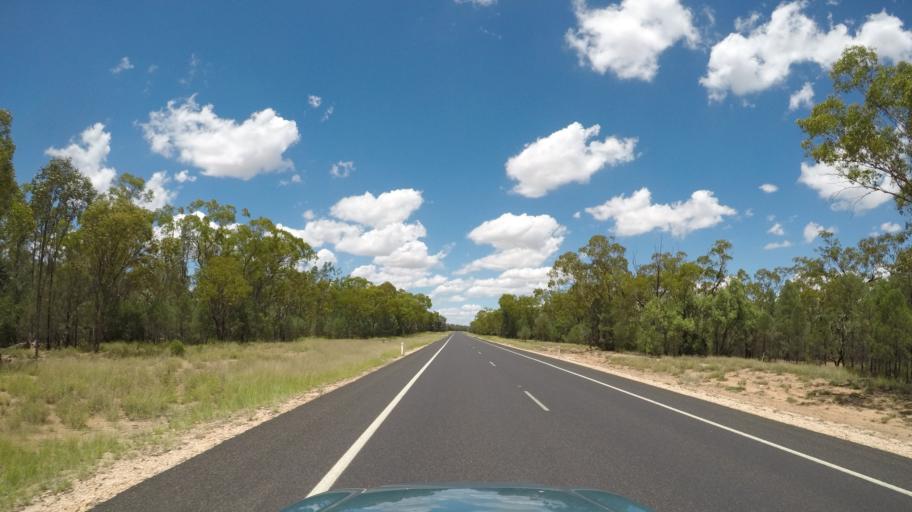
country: AU
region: Queensland
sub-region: Goondiwindi
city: Goondiwindi
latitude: -28.1012
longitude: 150.7241
